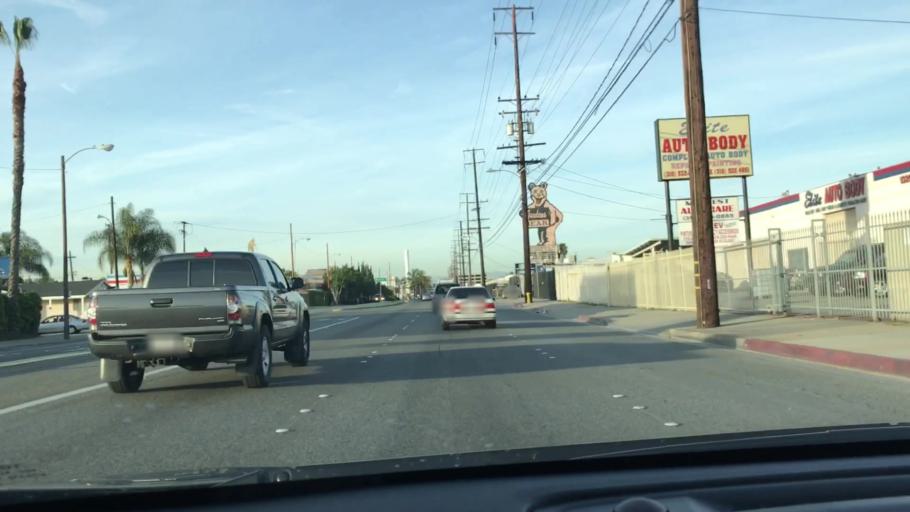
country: US
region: California
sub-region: Los Angeles County
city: Alondra Park
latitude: 33.9119
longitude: -118.3265
